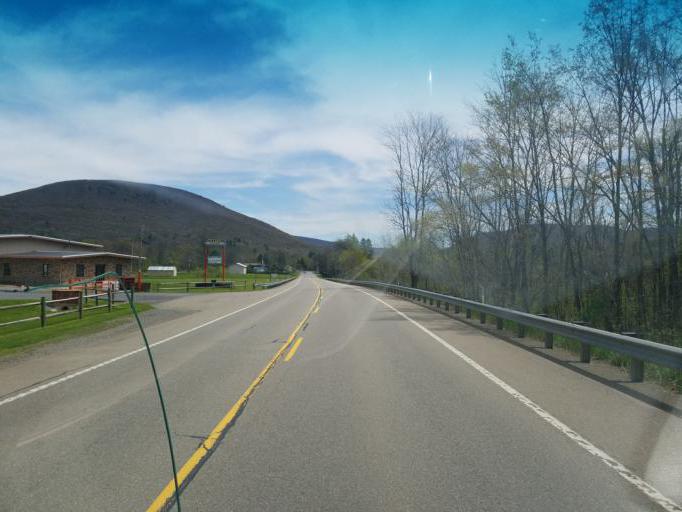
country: US
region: Pennsylvania
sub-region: Potter County
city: Galeton
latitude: 41.7435
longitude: -77.6082
